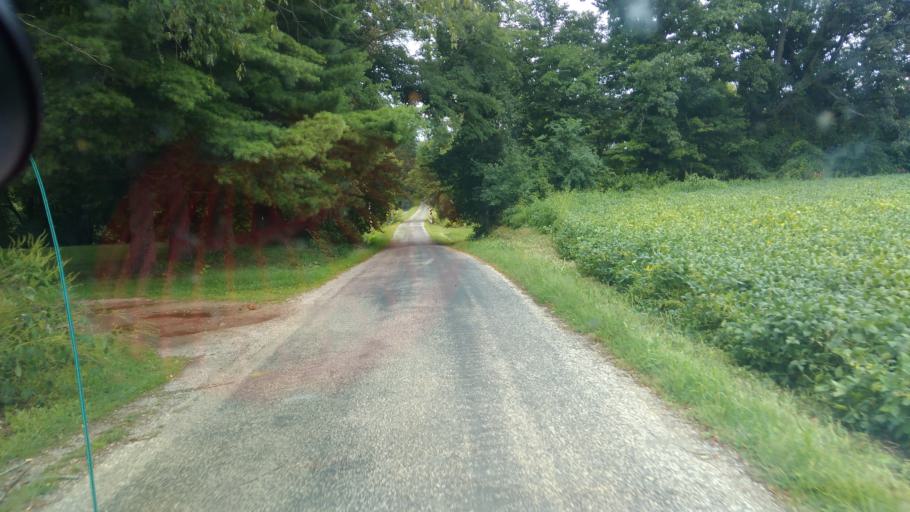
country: US
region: Ohio
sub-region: Richland County
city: Lincoln Heights
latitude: 40.8214
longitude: -82.4069
